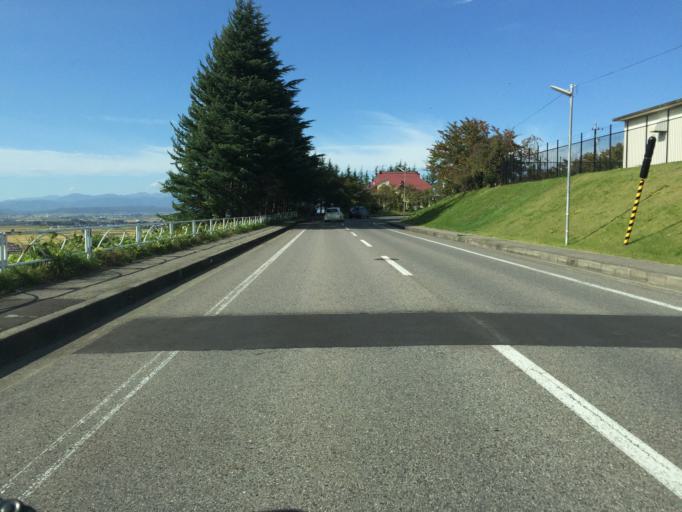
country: JP
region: Fukushima
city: Kitakata
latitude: 37.5269
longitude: 139.9540
